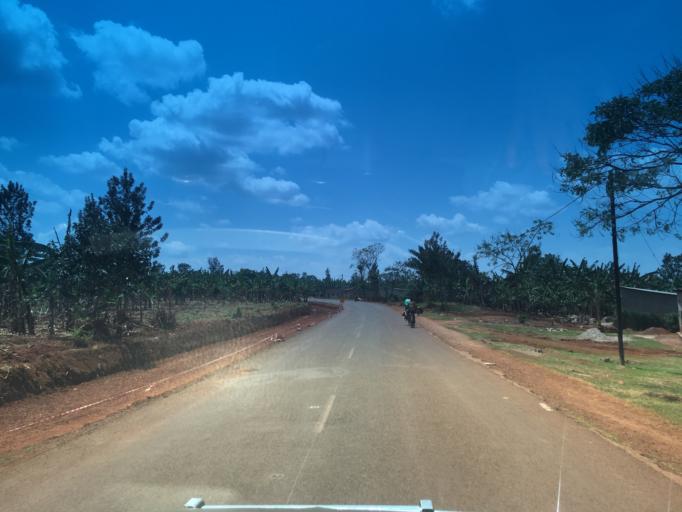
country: RW
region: Eastern Province
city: Kibungo
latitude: -2.2779
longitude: 30.5958
